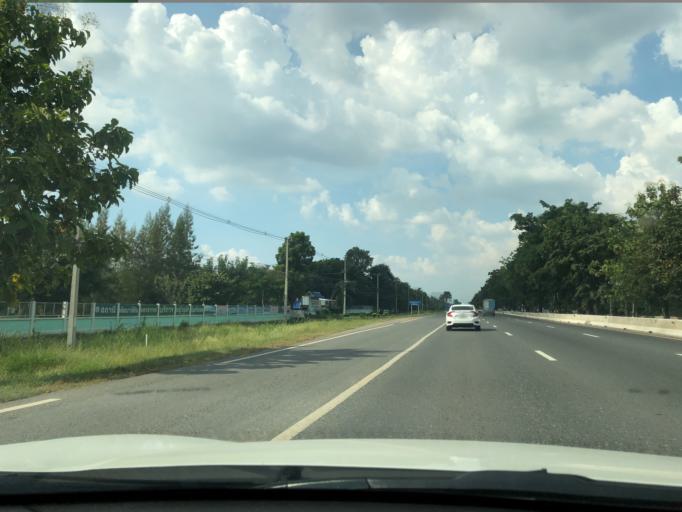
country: TH
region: Nakhon Sawan
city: Krok Phra
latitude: 15.5819
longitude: 100.1243
